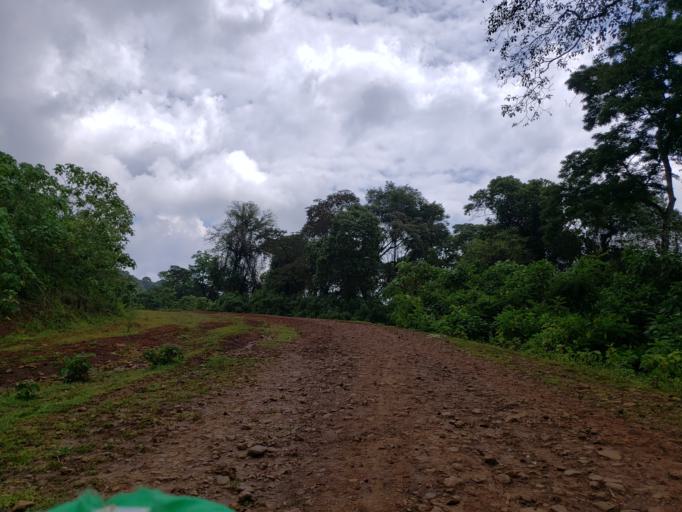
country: ET
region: Oromiya
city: Dodola
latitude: 6.4871
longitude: 39.4989
